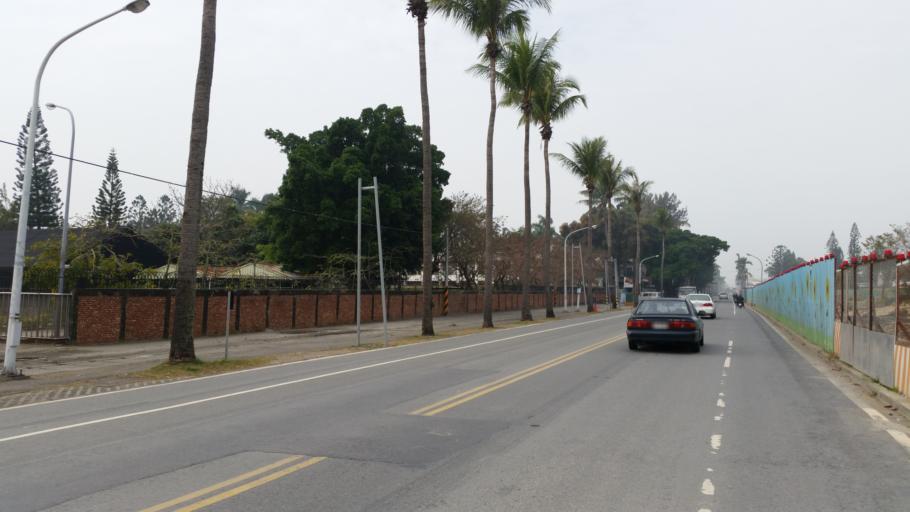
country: TW
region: Taiwan
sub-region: Tainan
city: Tainan
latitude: 22.9649
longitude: 120.2243
